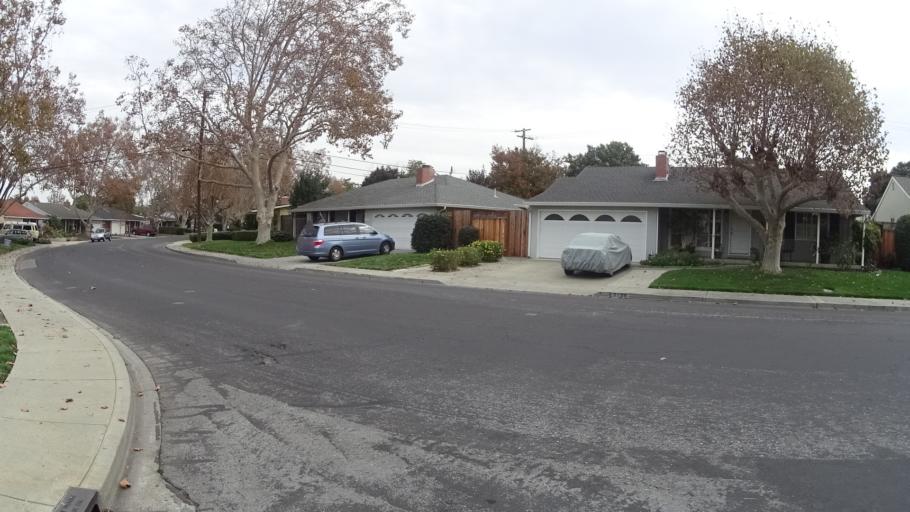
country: US
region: California
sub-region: Santa Clara County
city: Santa Clara
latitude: 37.3357
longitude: -121.9564
